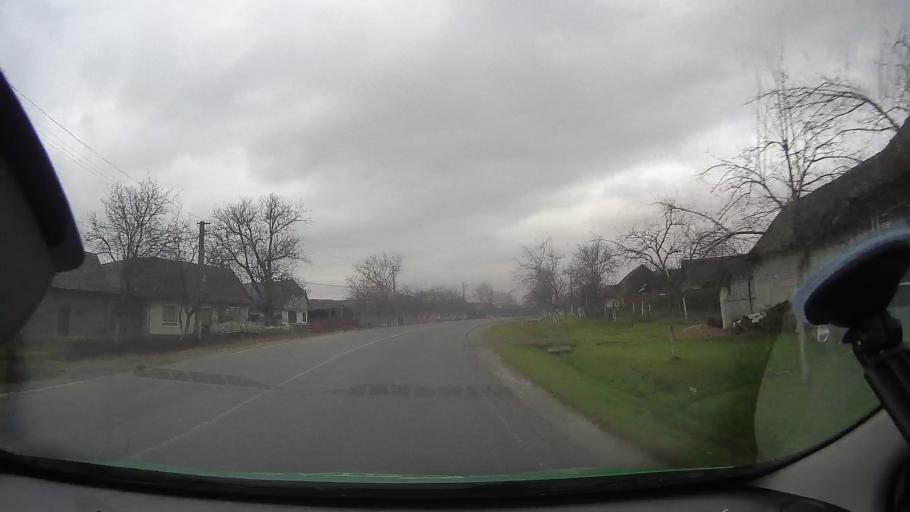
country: RO
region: Arad
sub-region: Comuna Almas
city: Almas
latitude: 46.2902
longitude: 22.2233
